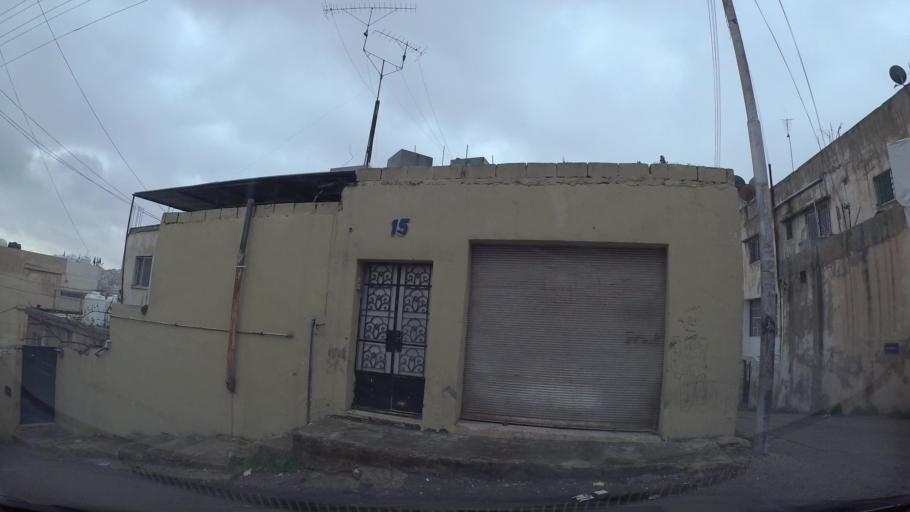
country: JO
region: Amman
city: Amman
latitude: 31.9509
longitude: 35.9116
